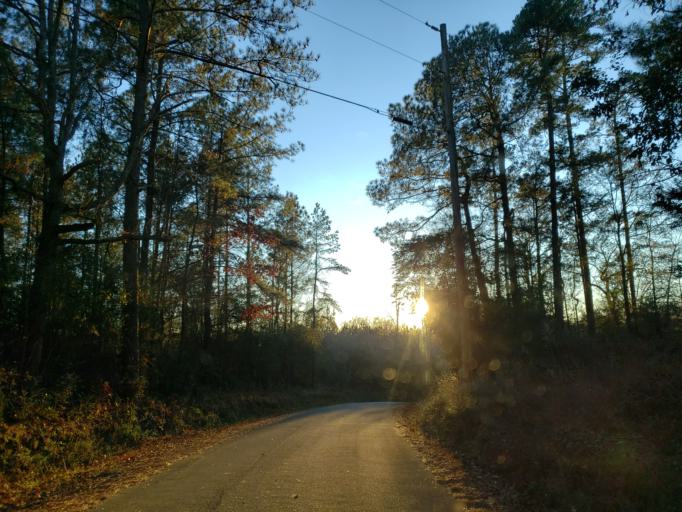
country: US
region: Mississippi
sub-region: Covington County
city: Collins
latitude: 31.5704
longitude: -89.4423
